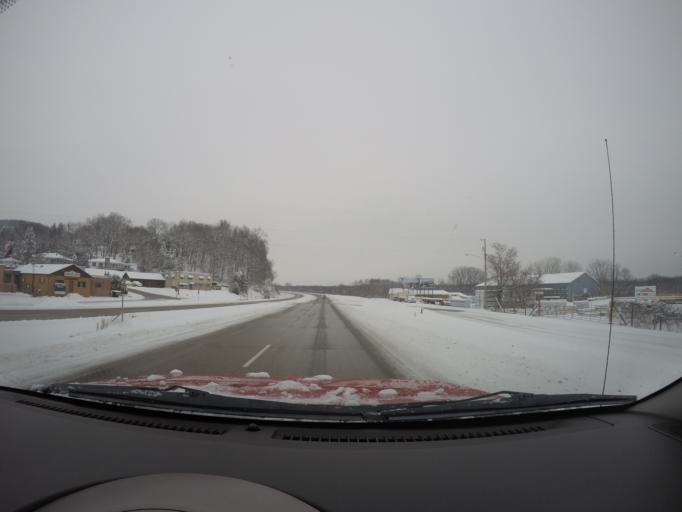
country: US
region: Minnesota
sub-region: Houston County
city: La Crescent
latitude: 43.8341
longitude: -91.3008
